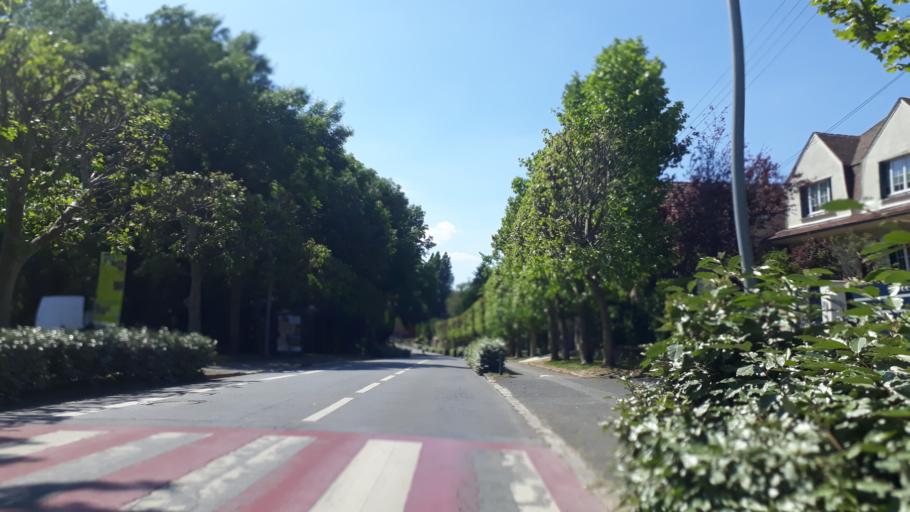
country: FR
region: Ile-de-France
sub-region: Departement de l'Essonne
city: Villebon-sur-Yvette
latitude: 48.7037
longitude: 2.2264
